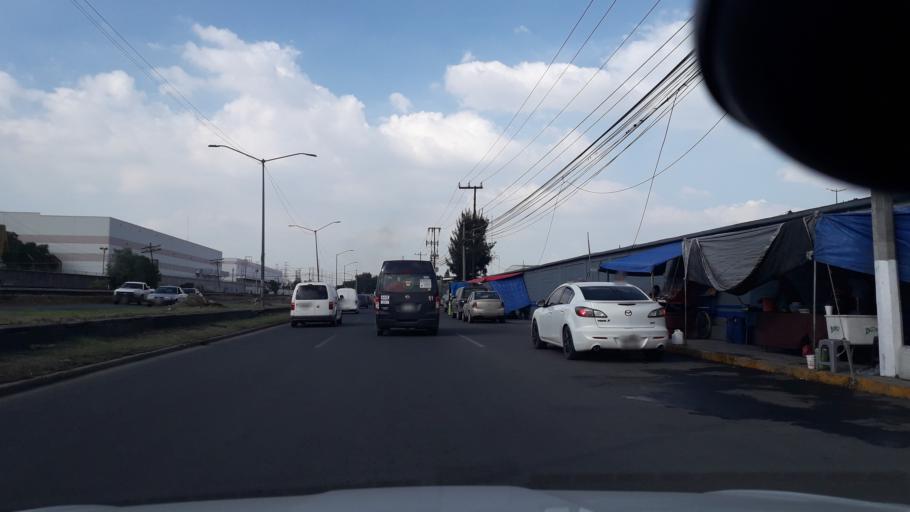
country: MX
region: Mexico
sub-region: Tultitlan
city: Buenavista
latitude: 19.6281
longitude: -99.1848
